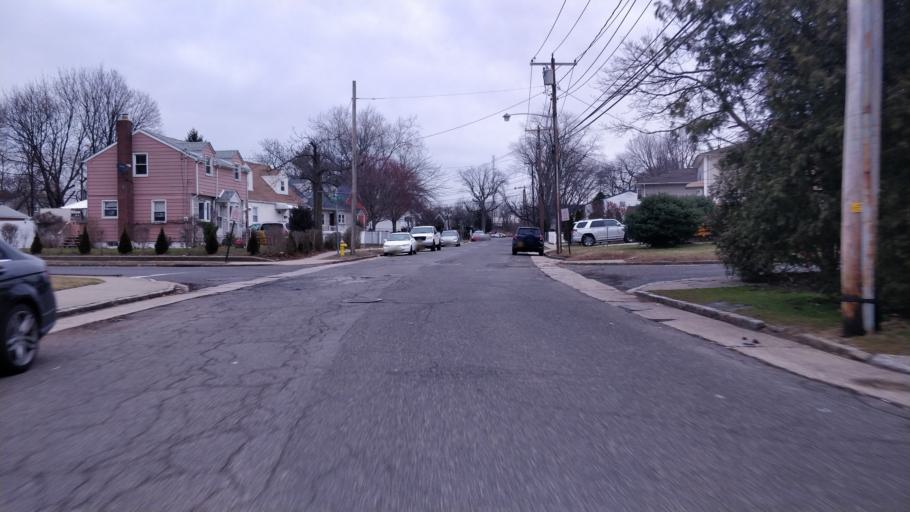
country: US
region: New York
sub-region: Nassau County
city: New Cassel
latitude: 40.7603
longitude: -73.5586
